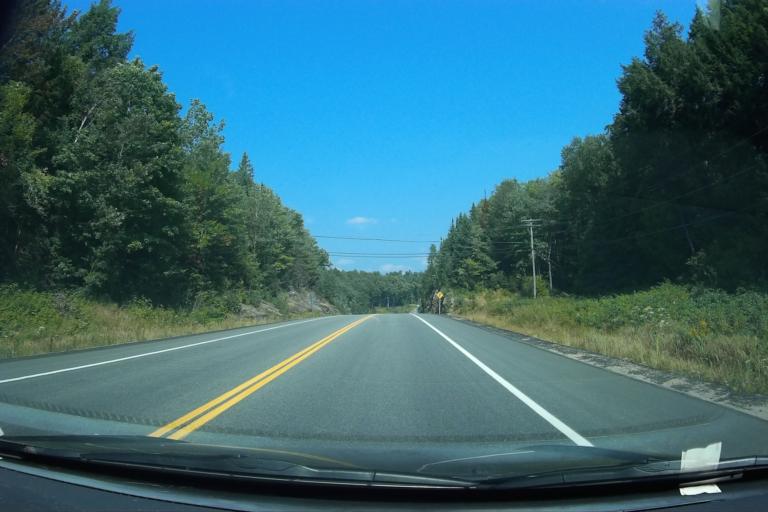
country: CA
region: Ontario
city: Huntsville
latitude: 45.5344
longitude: -78.7031
